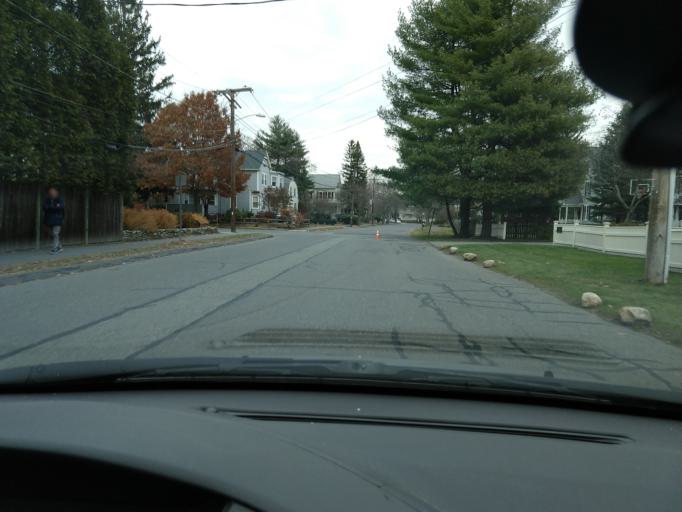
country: US
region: Massachusetts
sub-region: Middlesex County
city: Lexington
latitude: 42.4459
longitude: -71.2338
